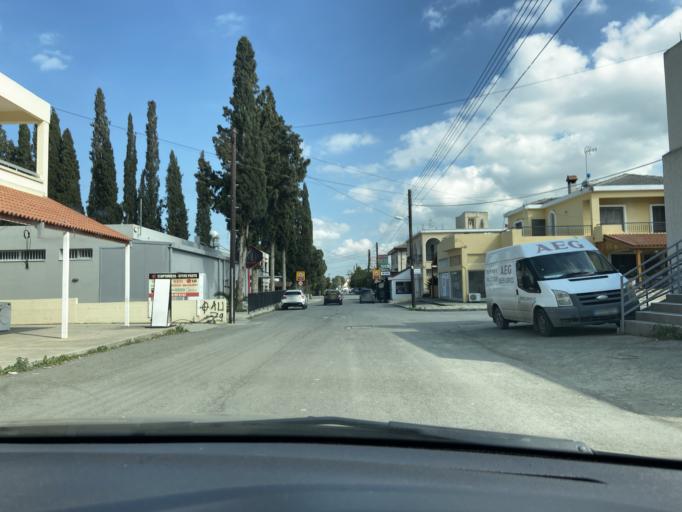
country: CY
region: Lefkosia
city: Alampra
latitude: 35.0140
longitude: 33.3916
